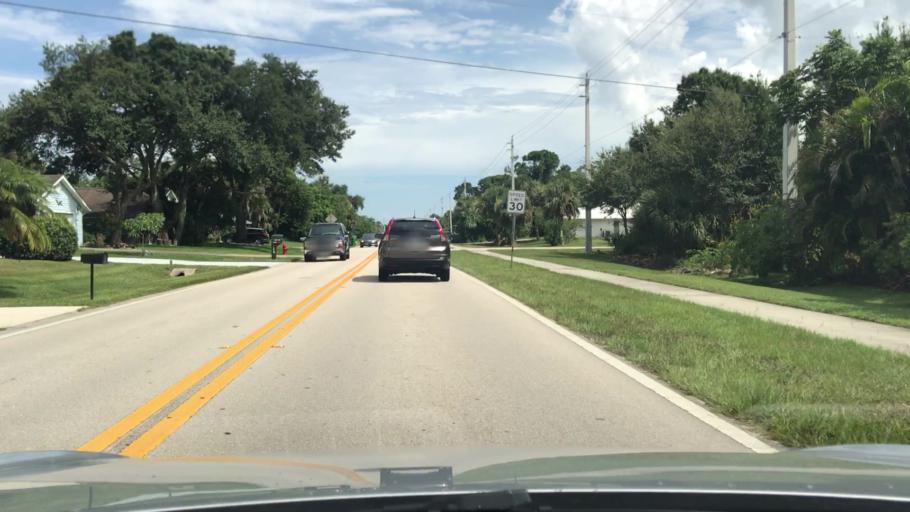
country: US
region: Florida
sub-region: Indian River County
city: Sebastian
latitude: 27.7642
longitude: -80.4759
